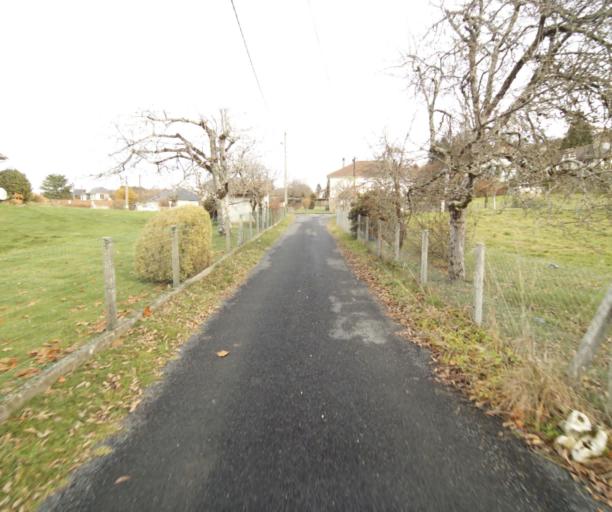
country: FR
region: Limousin
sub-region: Departement de la Correze
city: Saint-Mexant
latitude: 45.2690
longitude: 1.6792
